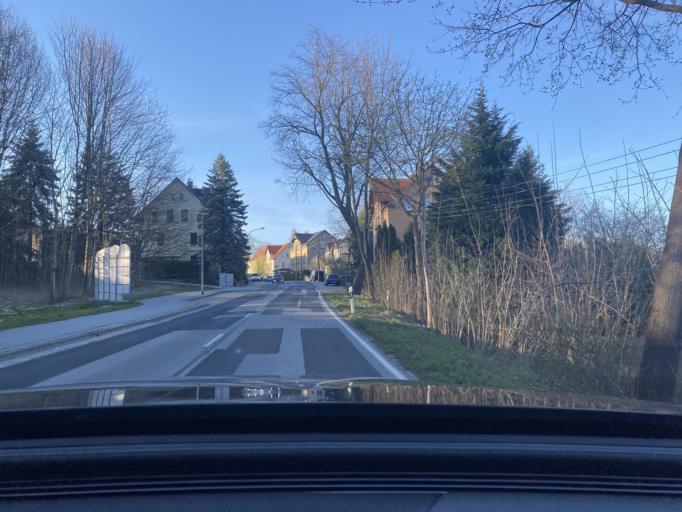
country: DE
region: Saxony
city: Schirgiswalde
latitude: 51.0837
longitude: 14.4259
